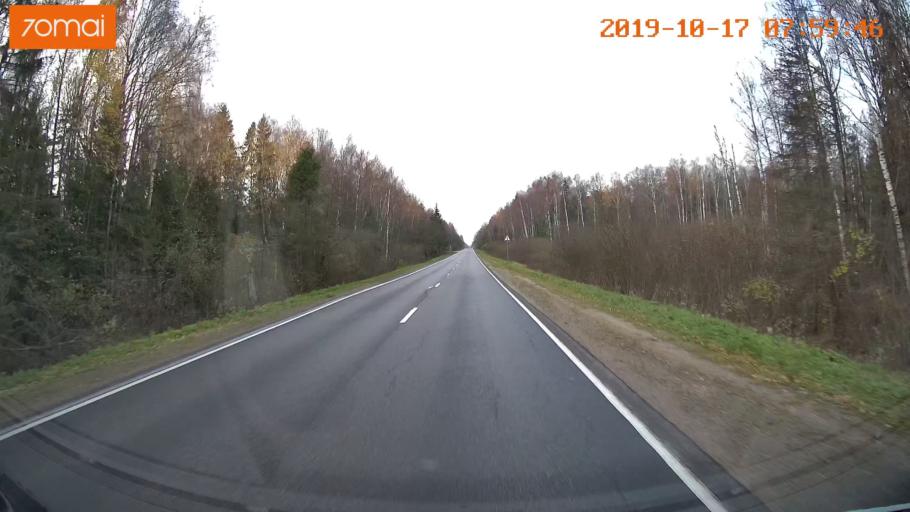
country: RU
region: Vladimir
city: Bavleny
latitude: 56.3900
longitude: 39.5317
